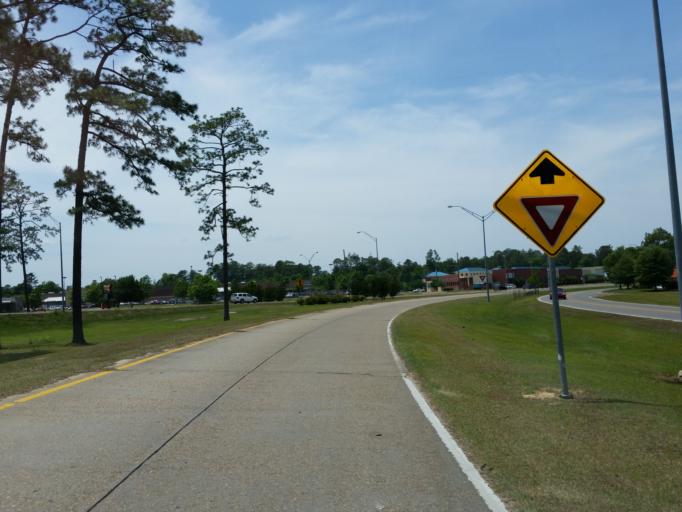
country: US
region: Mississippi
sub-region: Forrest County
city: Hattiesburg
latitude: 31.3088
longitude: -89.3170
